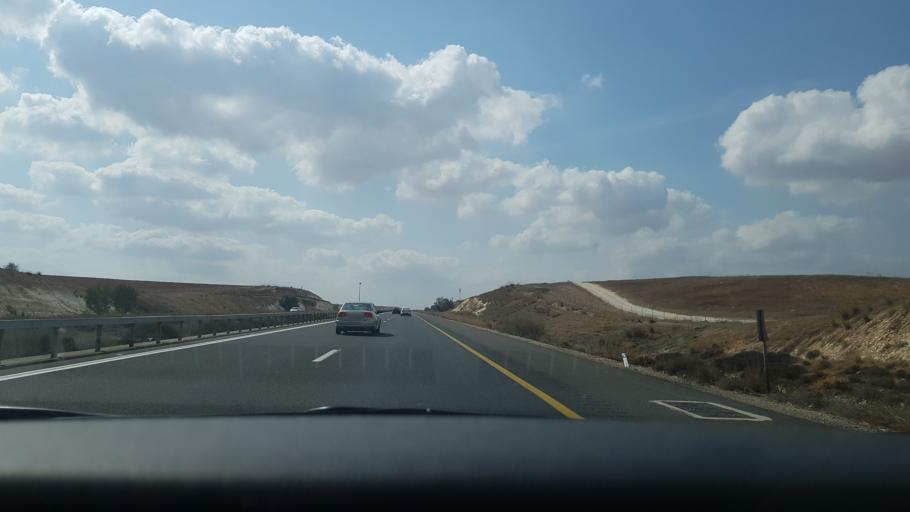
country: IL
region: Southern District
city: Qiryat Gat
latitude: 31.5514
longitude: 34.8001
